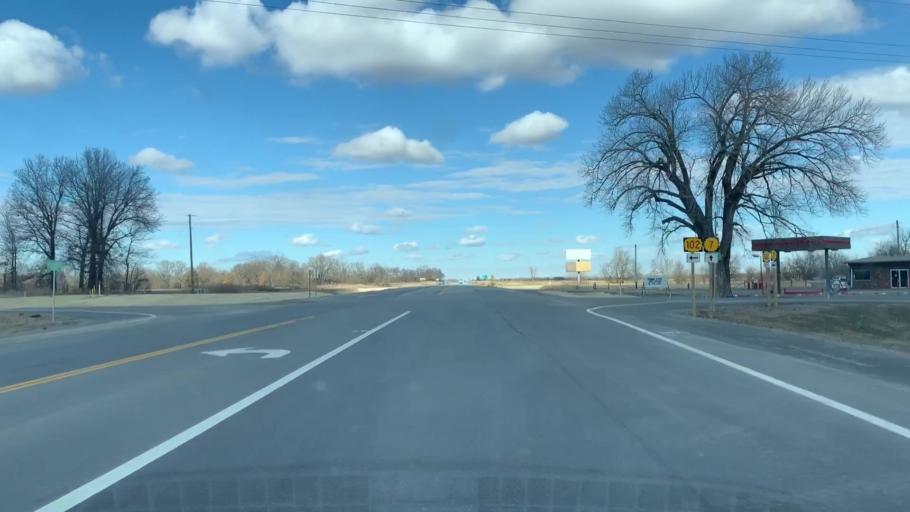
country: US
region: Kansas
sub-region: Cherokee County
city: Columbus
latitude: 37.2810
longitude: -94.8322
